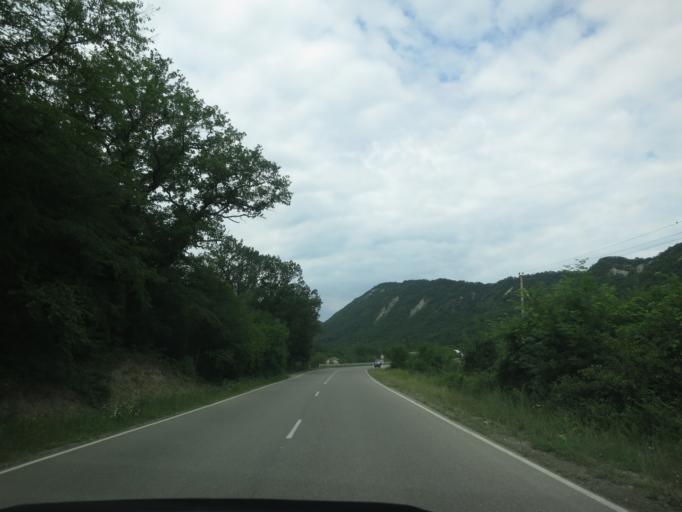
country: GE
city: Didi Lilo
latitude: 41.8073
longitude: 45.1388
